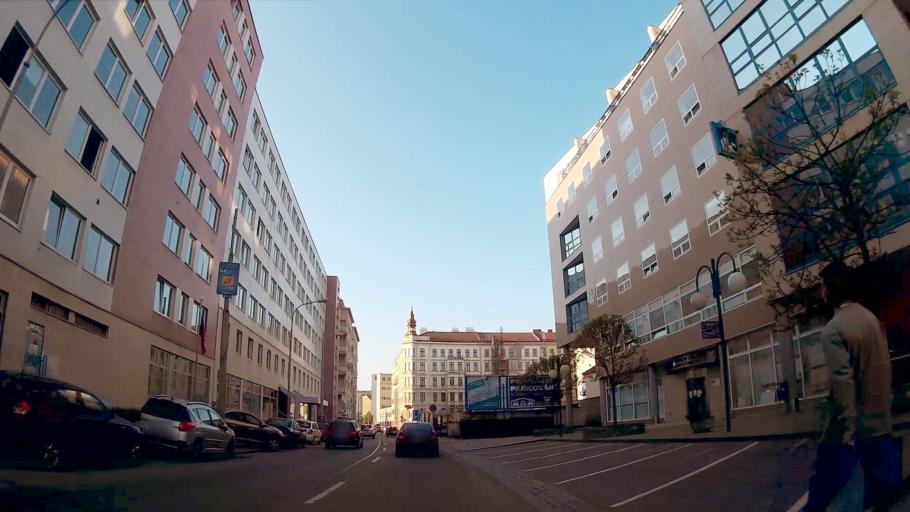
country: CZ
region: South Moravian
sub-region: Mesto Brno
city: Brno
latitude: 49.1996
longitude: 16.6148
